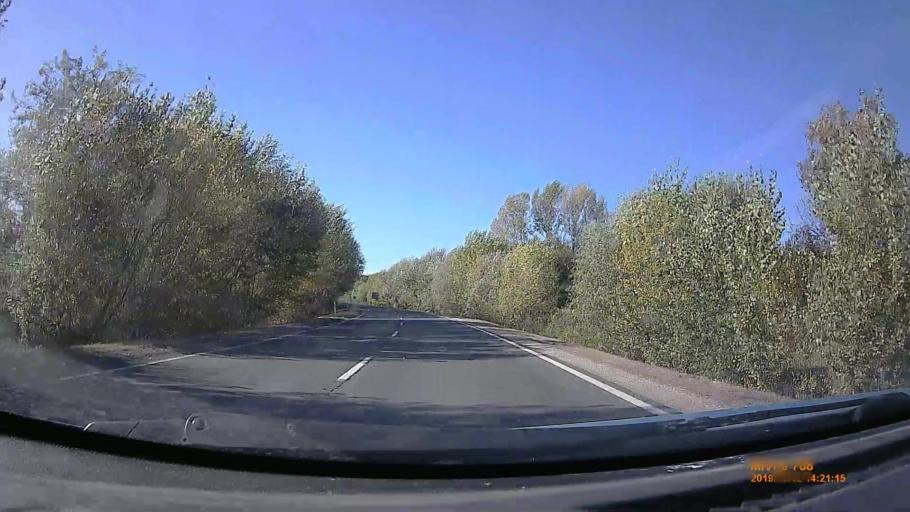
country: HU
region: Hajdu-Bihar
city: Biharkeresztes
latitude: 47.1381
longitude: 21.7376
